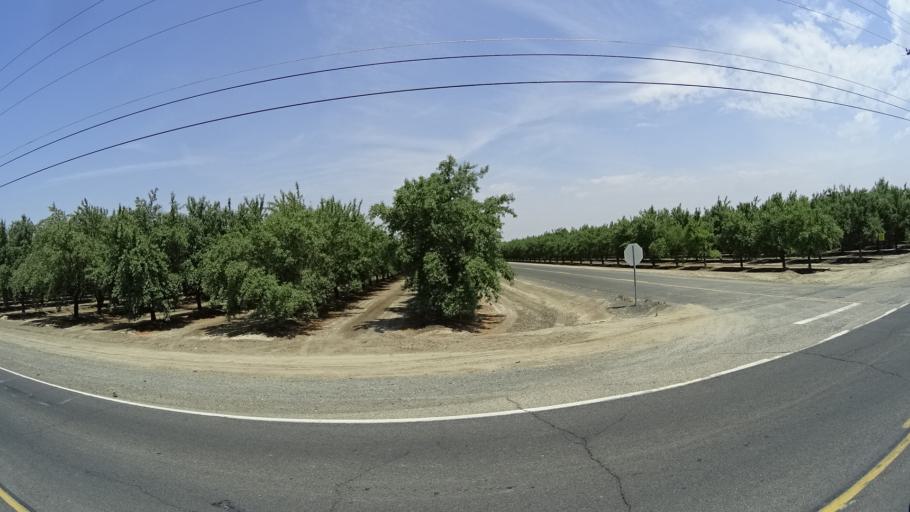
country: US
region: California
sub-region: Kings County
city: Armona
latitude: 36.3280
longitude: -119.7181
